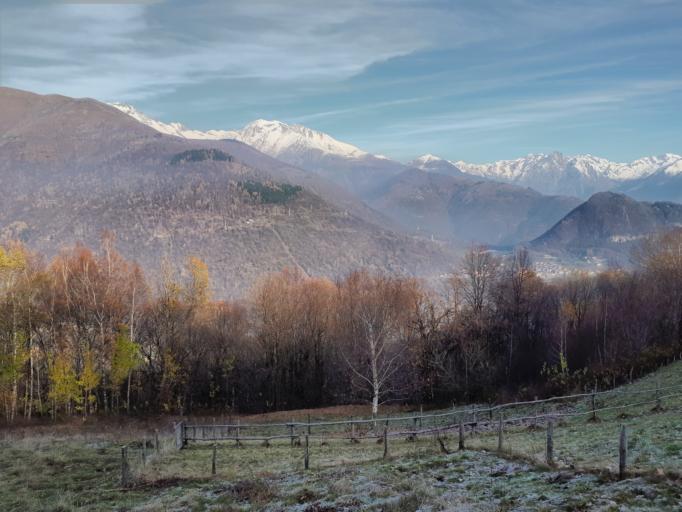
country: IT
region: Lombardy
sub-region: Provincia di Como
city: Dosso del Liro
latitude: 46.1526
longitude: 9.2703
